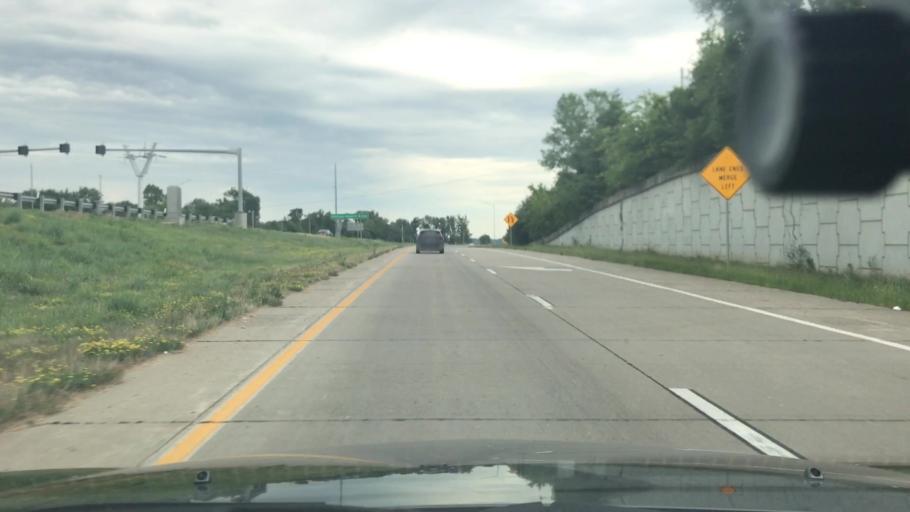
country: US
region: Missouri
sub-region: Saint Charles County
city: Saint Charles
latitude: 38.7424
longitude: -90.5285
